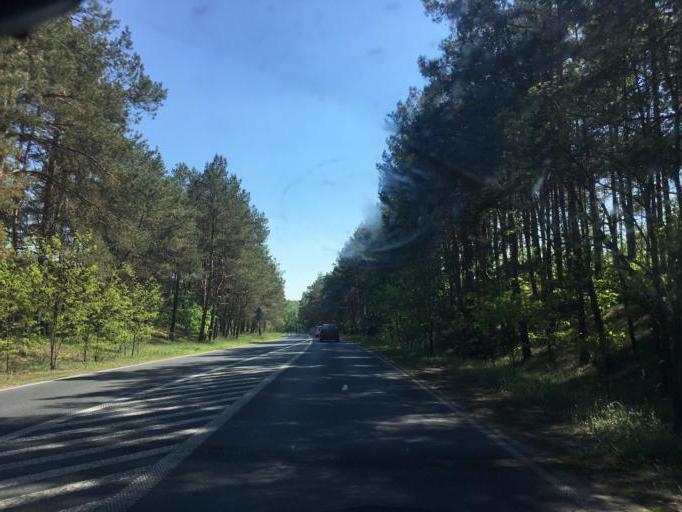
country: PL
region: Kujawsko-Pomorskie
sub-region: Bydgoszcz
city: Fordon
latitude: 53.0834
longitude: 18.1196
